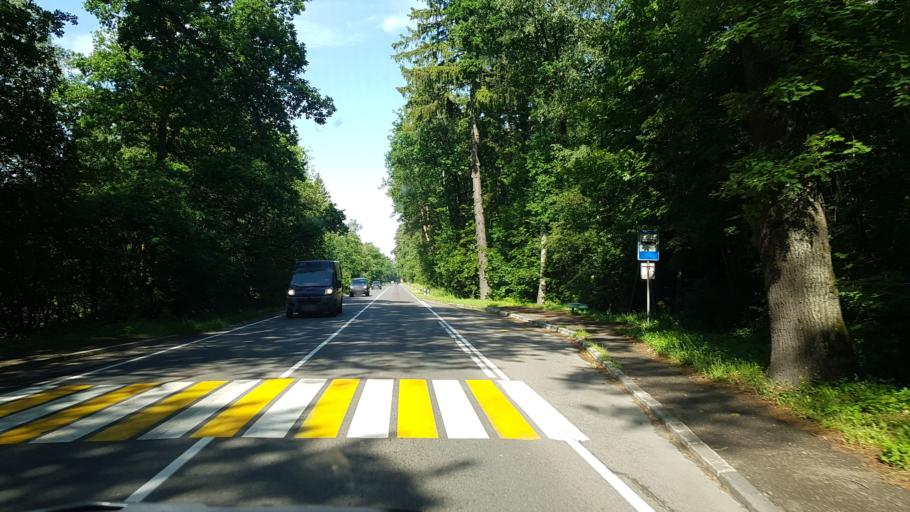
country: RU
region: Kaliningrad
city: Vzmorye
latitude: 54.7047
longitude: 20.2984
